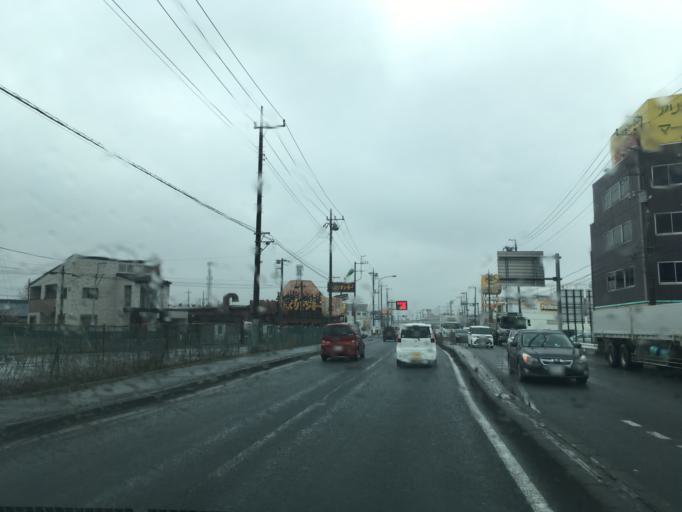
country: JP
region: Saitama
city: Koshigaya
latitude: 35.8727
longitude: 139.7783
